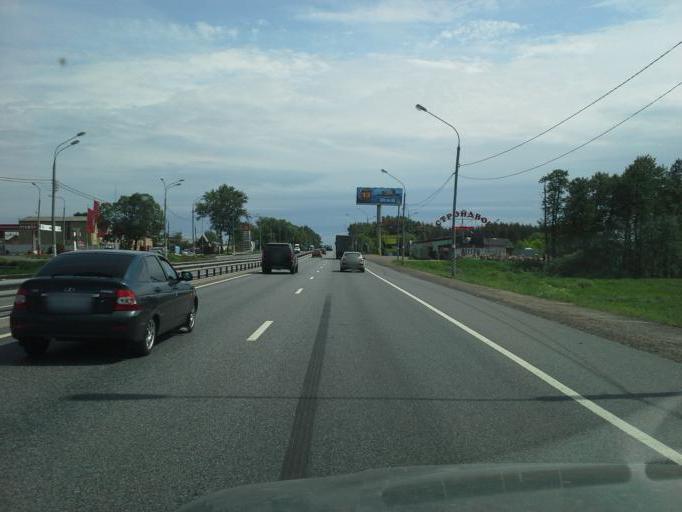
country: RU
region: Moskovskaya
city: Vishnyakovskiye Dachi
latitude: 55.8153
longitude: 38.1290
